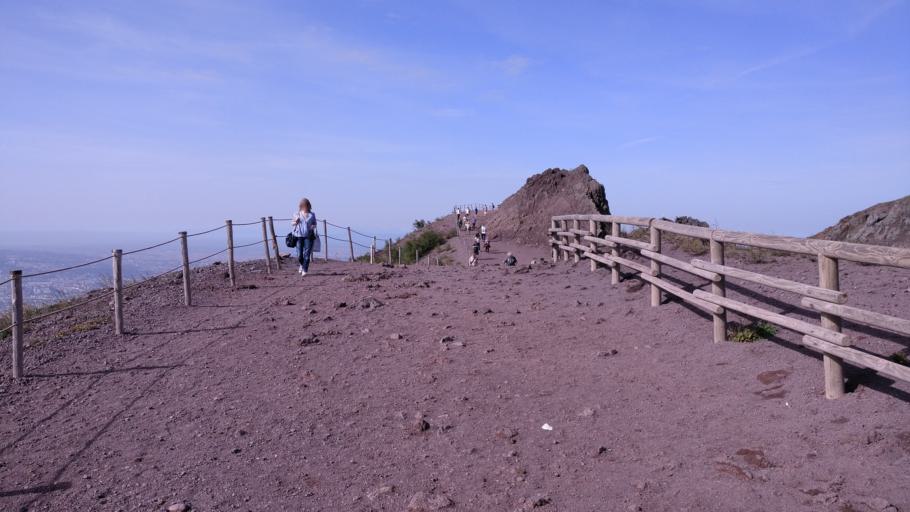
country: IT
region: Campania
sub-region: Provincia di Napoli
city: Torre del Greco
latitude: 40.8196
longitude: 14.4240
